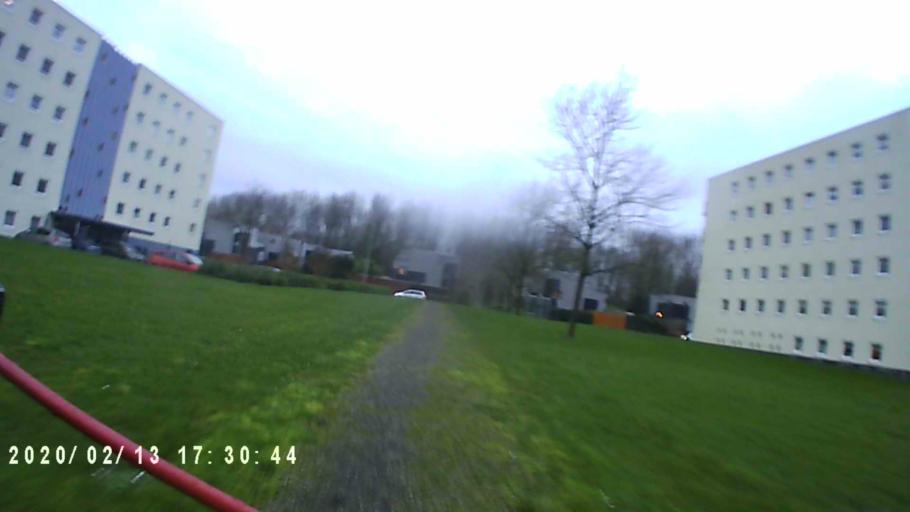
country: NL
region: Groningen
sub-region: Gemeente Groningen
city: Groningen
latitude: 53.2224
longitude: 6.5187
